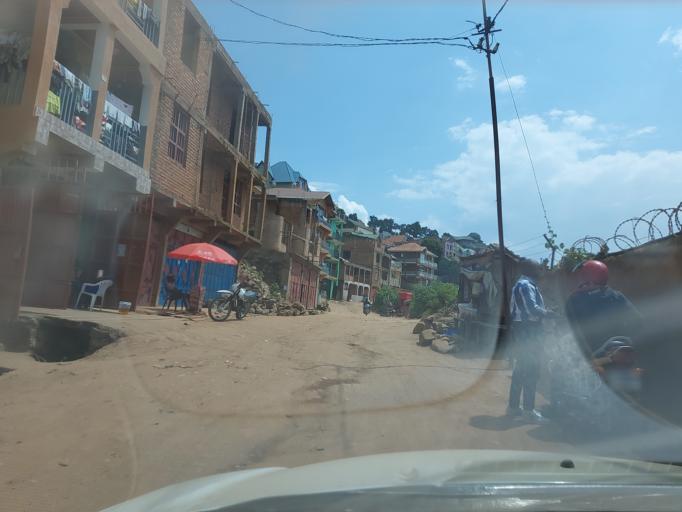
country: CD
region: South Kivu
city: Bukavu
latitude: -2.5000
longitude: 28.8619
